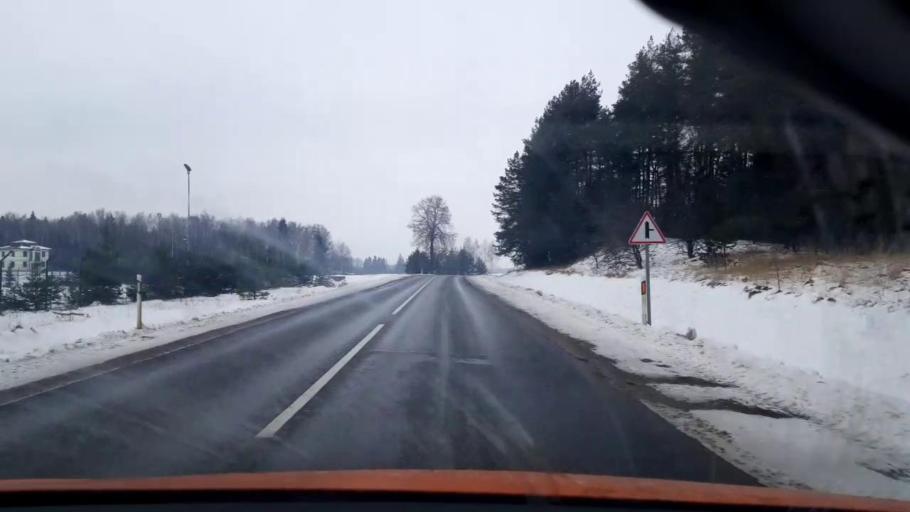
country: LT
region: Vilnius County
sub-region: Vilnius
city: Fabijoniskes
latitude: 54.8532
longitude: 25.2666
